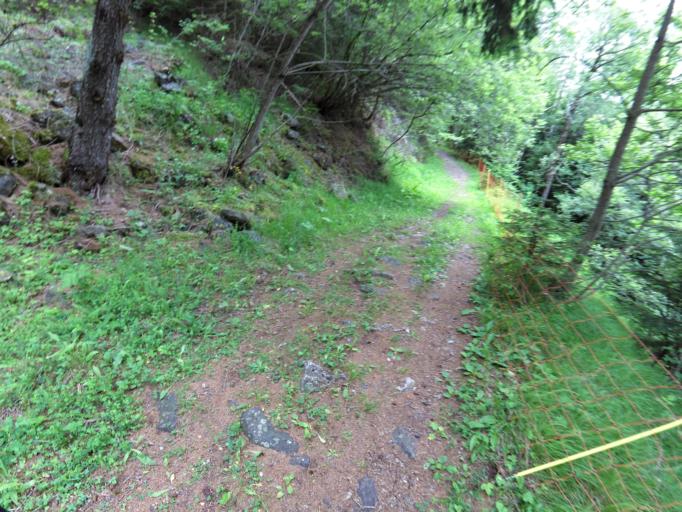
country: IT
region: Trentino-Alto Adige
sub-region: Bolzano
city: Siusi
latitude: 46.5401
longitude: 11.5894
